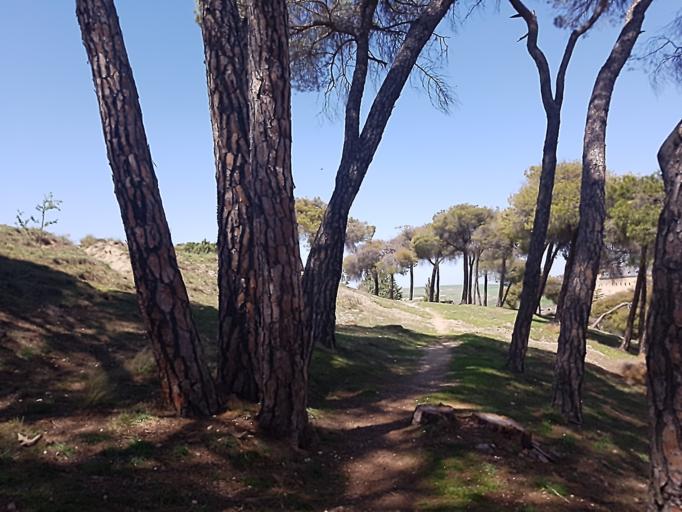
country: ES
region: Castille and Leon
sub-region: Provincia de Segovia
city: Segovia
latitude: 40.9495
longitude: -4.1312
